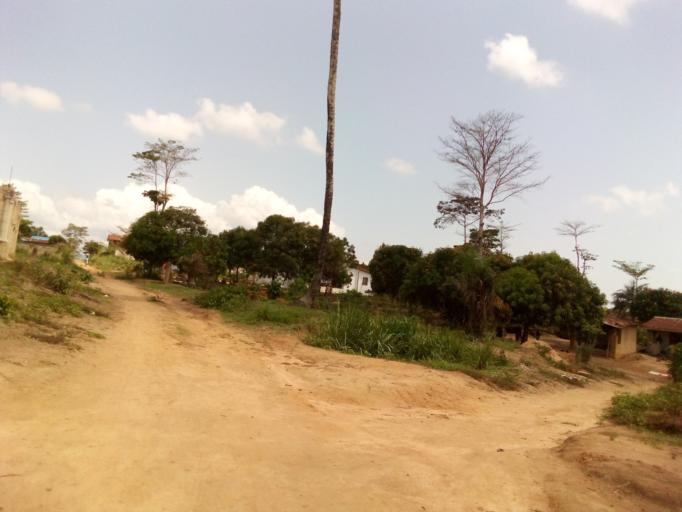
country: SL
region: Western Area
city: Waterloo
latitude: 8.3373
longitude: -13.0212
